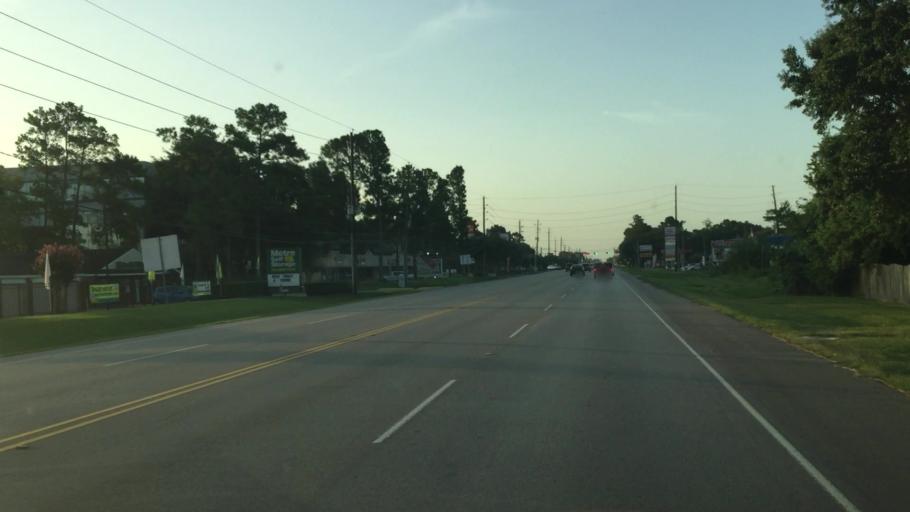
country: US
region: Texas
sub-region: Harris County
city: Hudson
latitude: 29.9847
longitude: -95.4994
